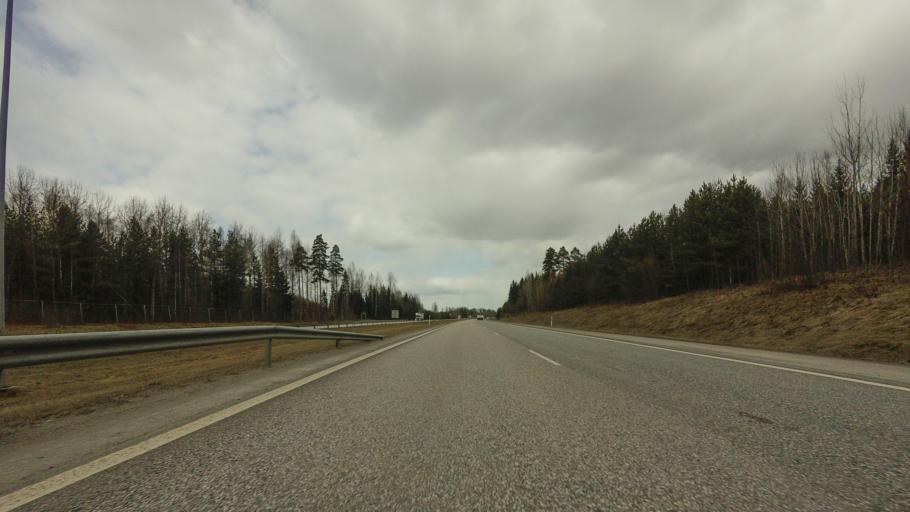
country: FI
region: Uusimaa
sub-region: Helsinki
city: Nurmijaervi
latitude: 60.3623
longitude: 24.8087
